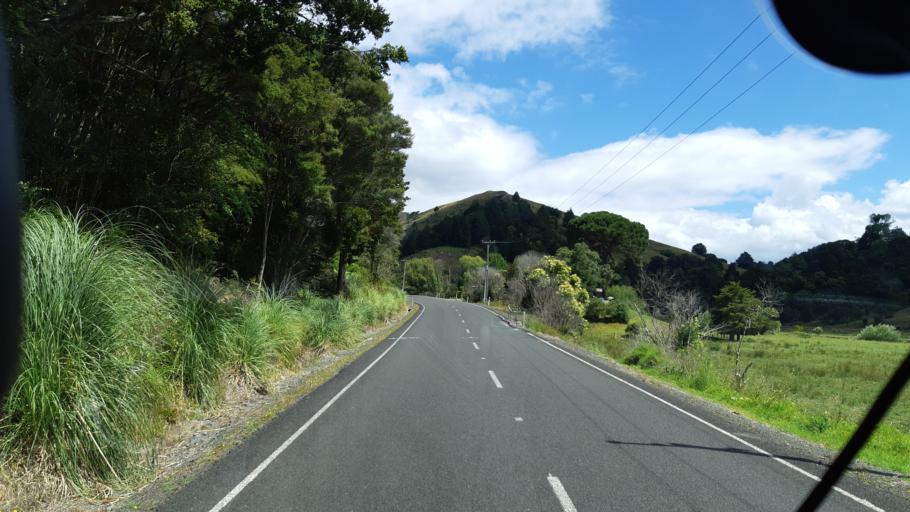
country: NZ
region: Northland
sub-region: Far North District
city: Taipa
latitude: -35.2680
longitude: 173.5036
